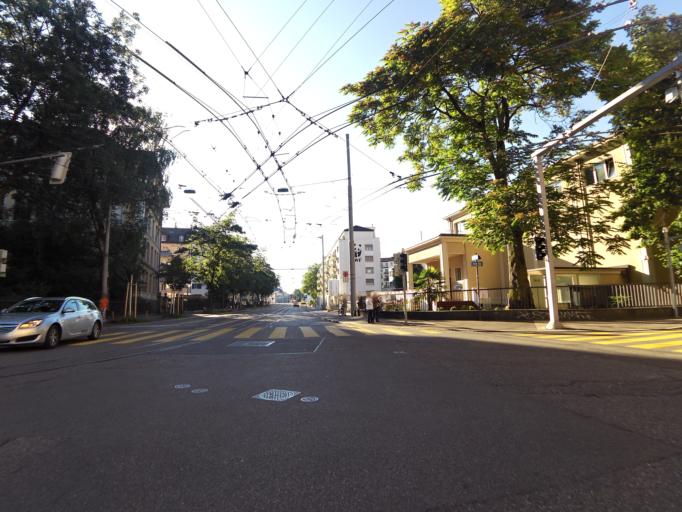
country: CH
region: Zurich
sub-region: Bezirk Zuerich
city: Aussersihl
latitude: 47.3787
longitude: 8.5232
